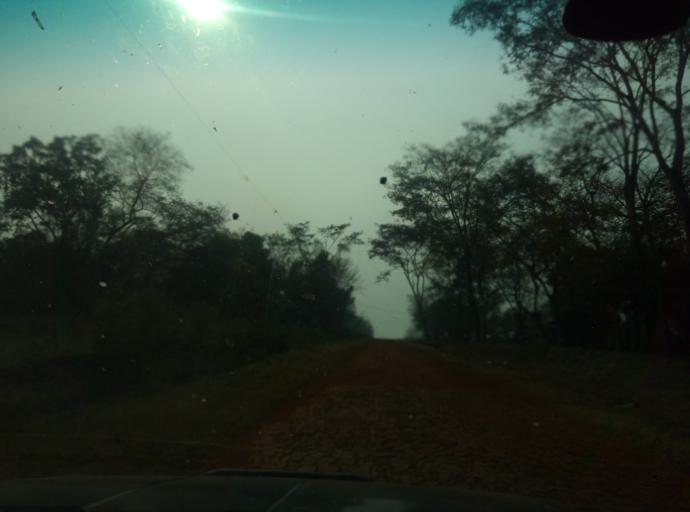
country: PY
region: Caaguazu
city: Carayao
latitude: -25.2039
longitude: -56.2408
